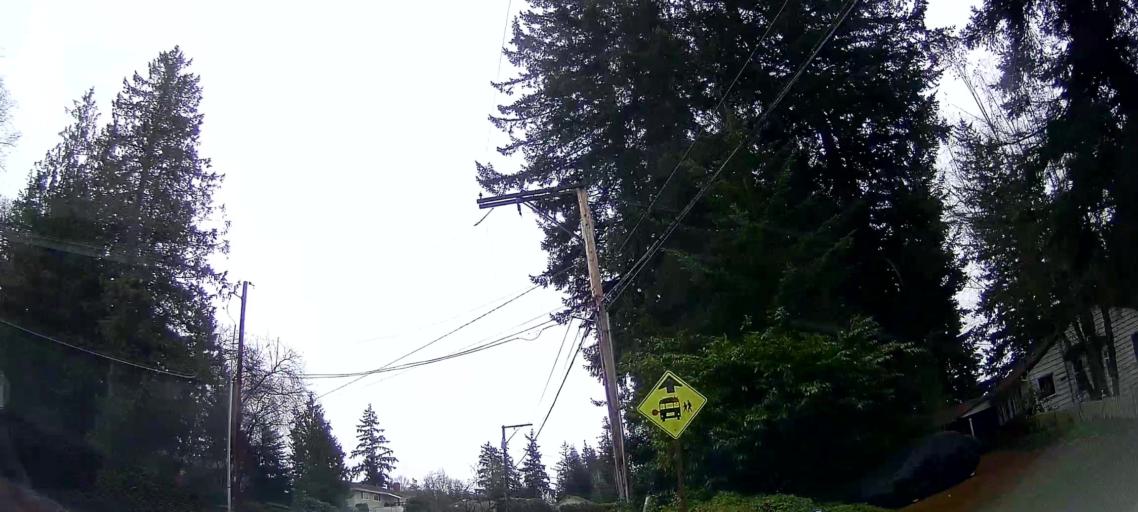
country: US
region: Washington
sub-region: Skagit County
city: Mount Vernon
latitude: 48.3970
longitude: -122.3226
